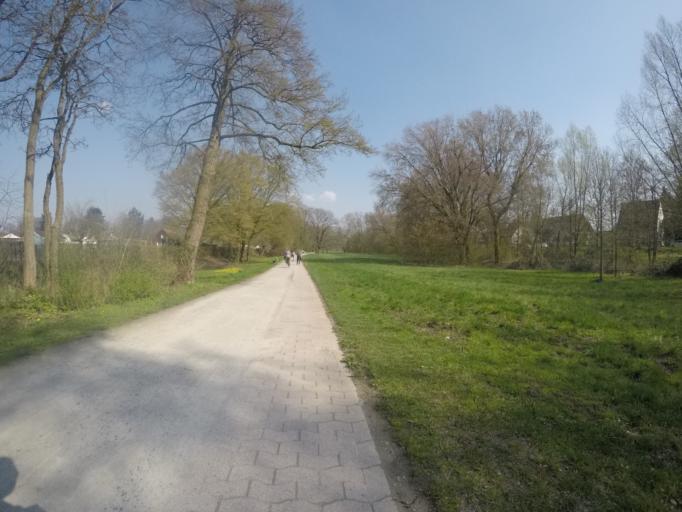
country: DE
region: North Rhine-Westphalia
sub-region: Regierungsbezirk Detmold
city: Bielefeld
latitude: 52.0272
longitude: 8.5810
